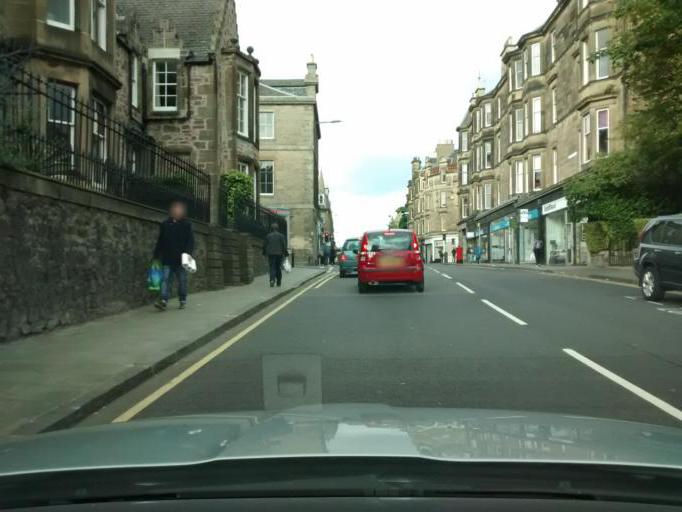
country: GB
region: Scotland
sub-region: Edinburgh
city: Edinburgh
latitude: 55.9313
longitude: -3.2100
